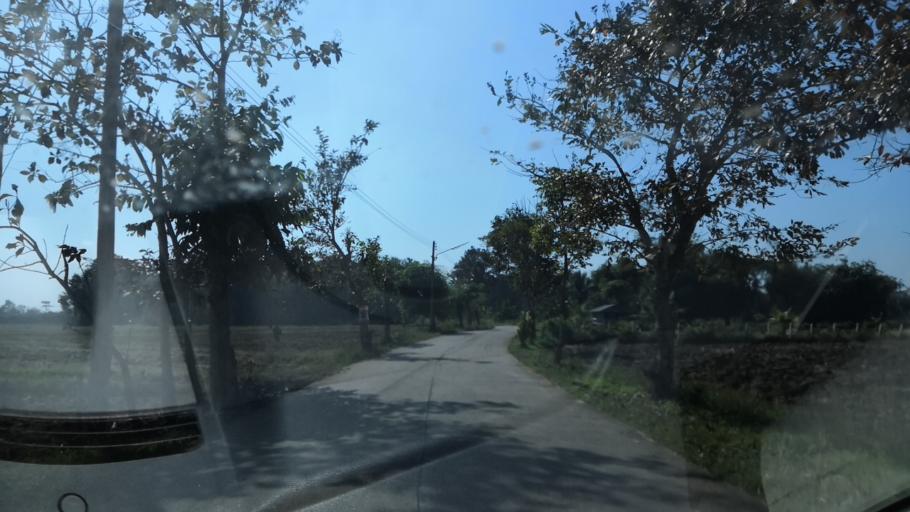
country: TH
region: Chiang Rai
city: Wiang Chai
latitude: 19.8840
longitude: 99.9433
